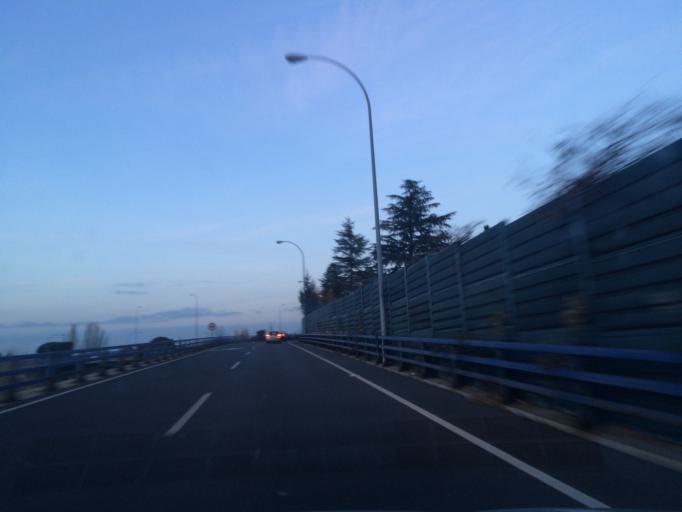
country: ES
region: Madrid
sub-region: Provincia de Madrid
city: Fuencarral-El Pardo
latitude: 40.4770
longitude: -3.7510
